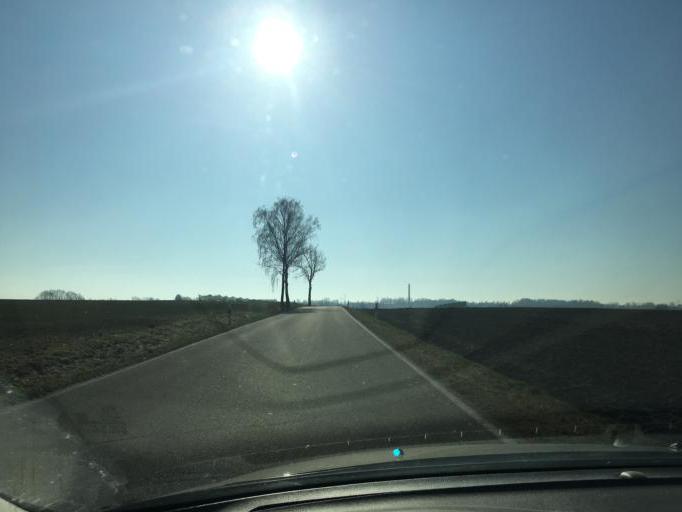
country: DE
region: Saxony
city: Narsdorf
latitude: 51.0236
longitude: 12.7099
